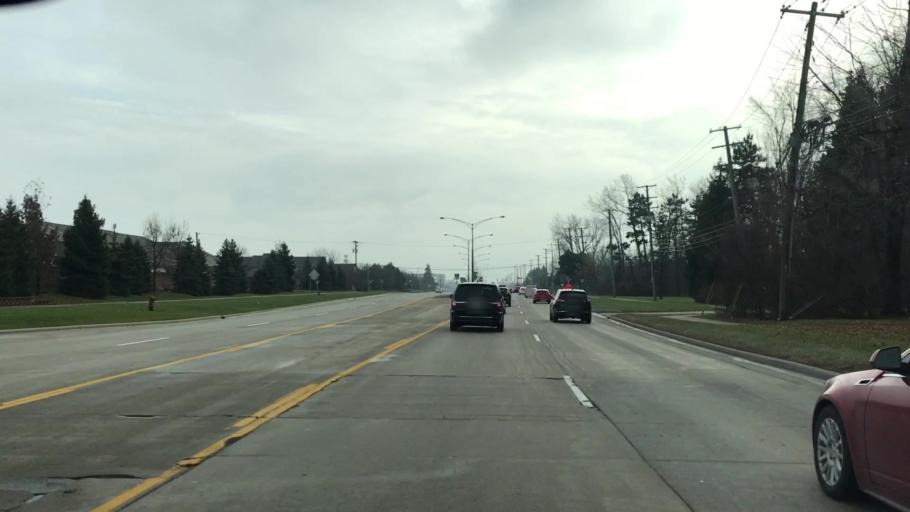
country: US
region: Michigan
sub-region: Oakland County
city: Troy
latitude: 42.5832
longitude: -83.1287
